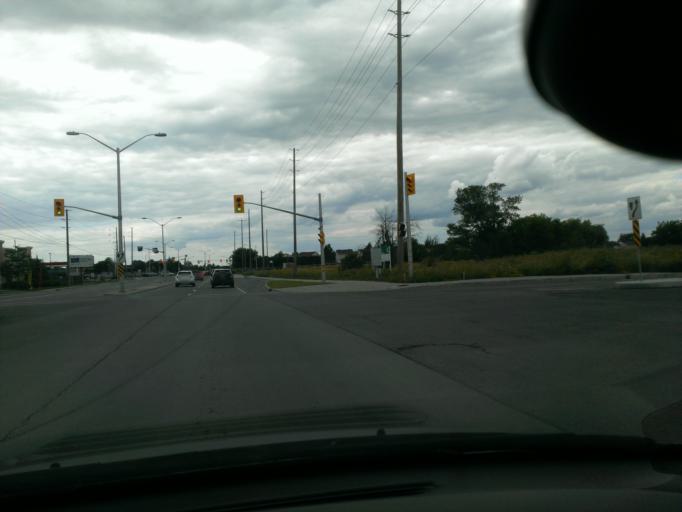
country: CA
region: Ontario
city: Ottawa
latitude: 45.4538
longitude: -75.5035
